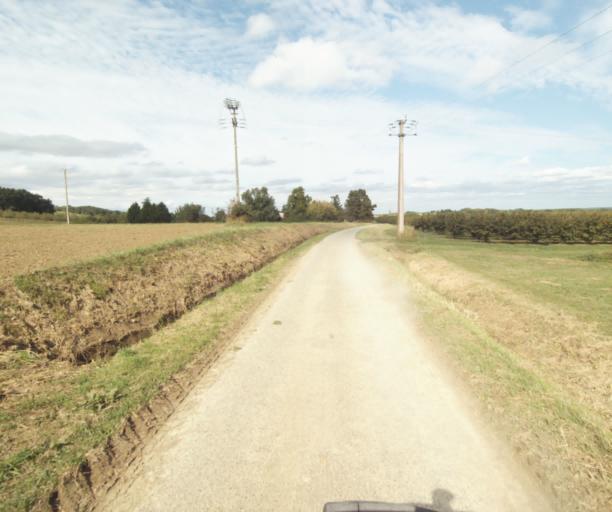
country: FR
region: Midi-Pyrenees
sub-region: Departement du Tarn-et-Garonne
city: Verdun-sur-Garonne
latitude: 43.8738
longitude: 1.1954
